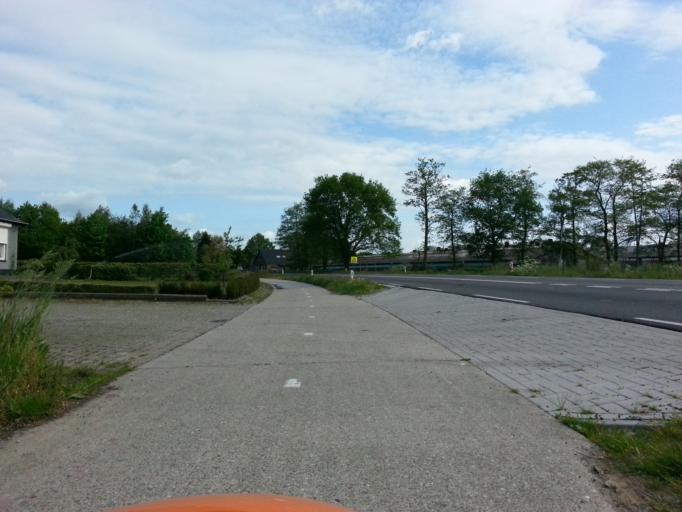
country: NL
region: Utrecht
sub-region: Gemeente Utrechtse Heuvelrug
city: Overberg
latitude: 52.0944
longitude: 5.5134
